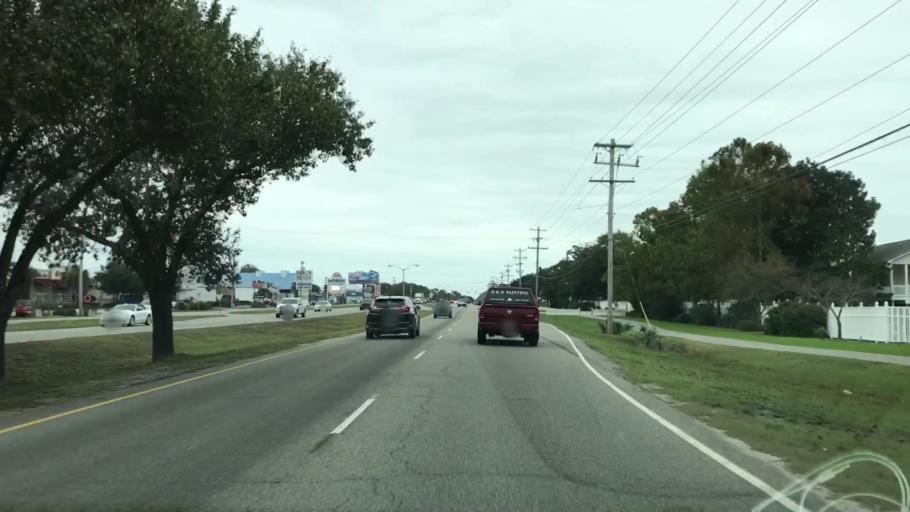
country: US
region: South Carolina
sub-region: Horry County
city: Surfside Beach
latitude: 33.6263
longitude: -78.9661
